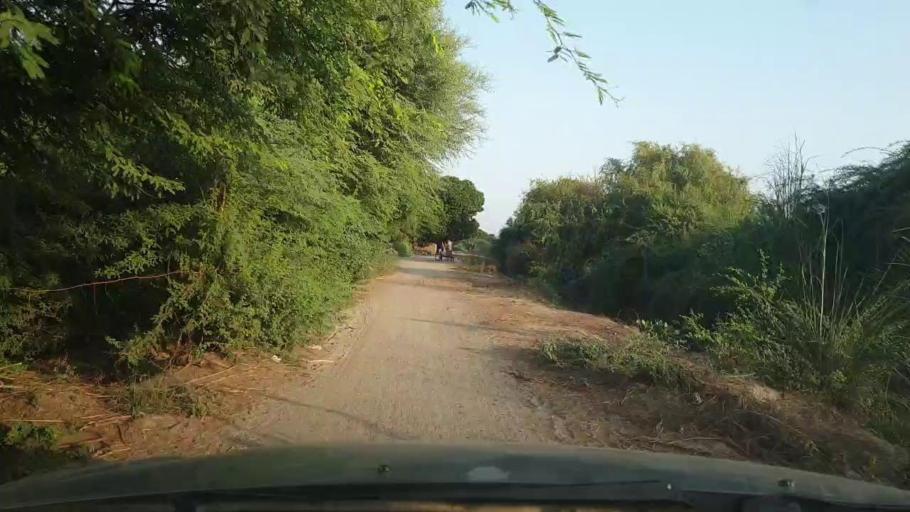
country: PK
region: Sindh
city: Tando Ghulam Ali
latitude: 25.1500
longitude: 68.9676
